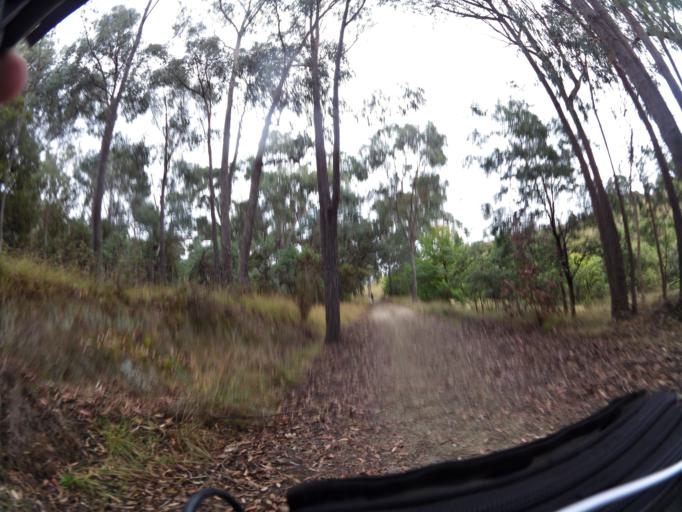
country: AU
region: New South Wales
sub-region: Greater Hume Shire
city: Holbrook
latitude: -36.1559
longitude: 147.4116
